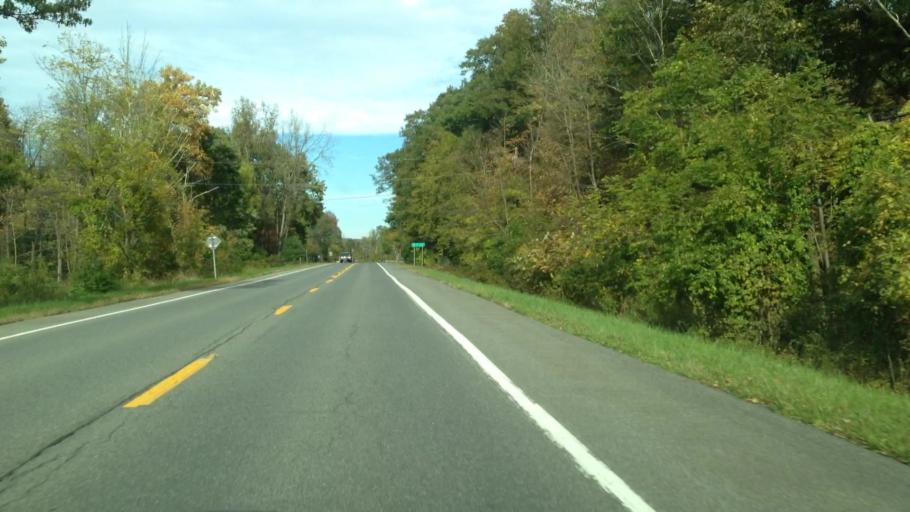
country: US
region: New York
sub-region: Ulster County
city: Port Ewen
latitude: 41.8791
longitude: -74.0217
